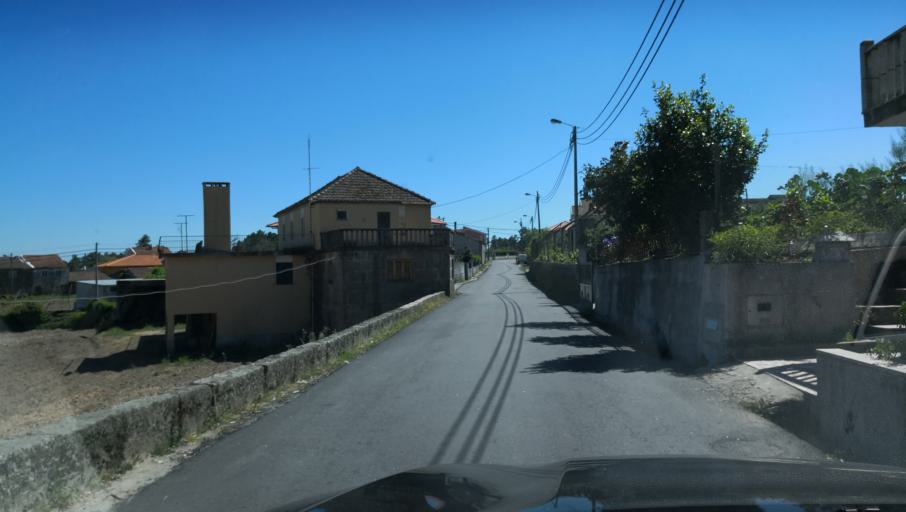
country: PT
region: Vila Real
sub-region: Vila Real
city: Vila Real
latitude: 41.2910
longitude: -7.6799
